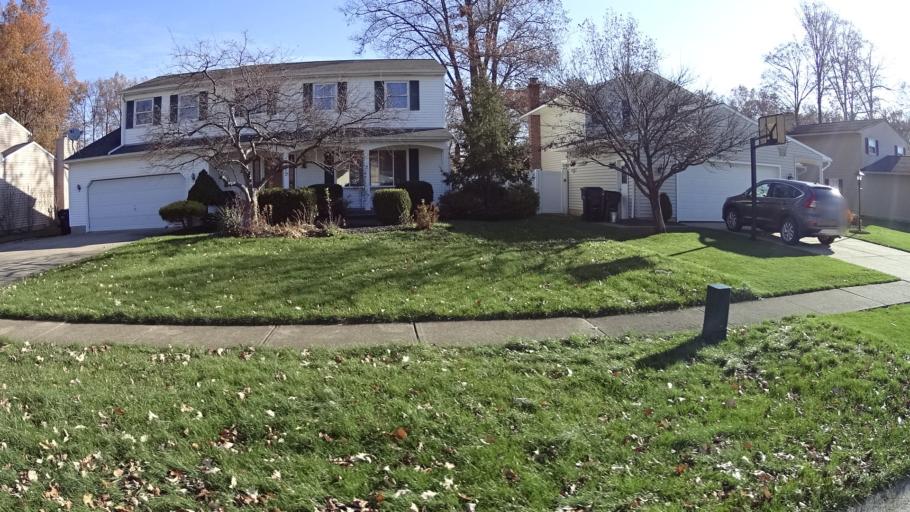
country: US
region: Ohio
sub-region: Lorain County
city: Sheffield
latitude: 41.3927
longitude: -82.0761
